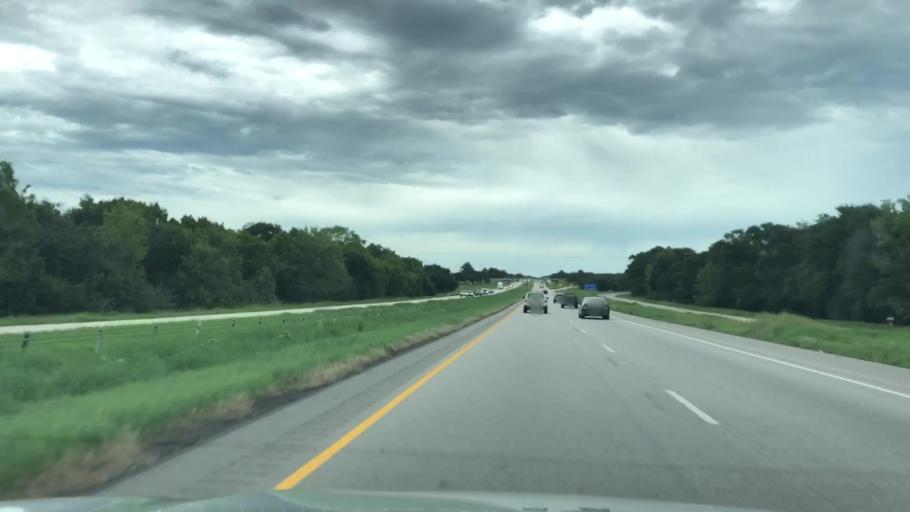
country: US
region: Texas
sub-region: Colorado County
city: Columbus
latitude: 29.6911
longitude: -96.6564
